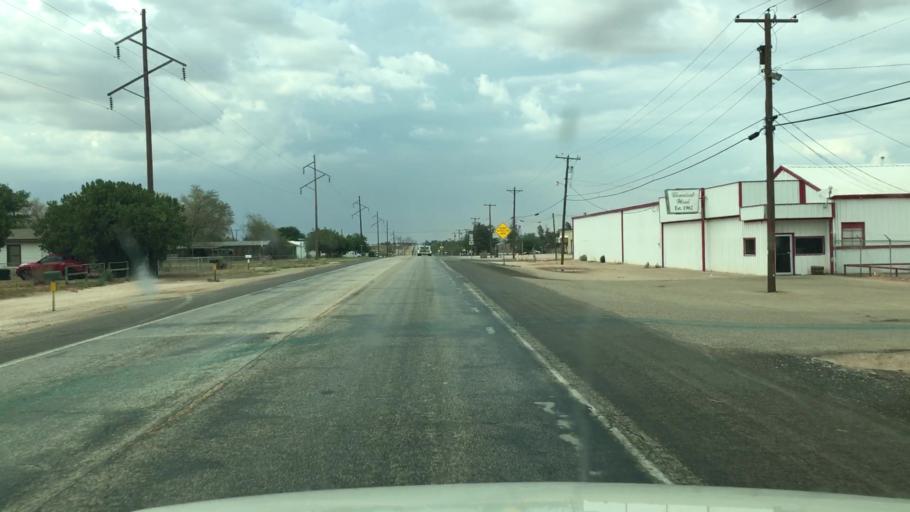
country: US
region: Texas
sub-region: Terry County
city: Brownfield
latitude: 33.1729
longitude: -102.2915
